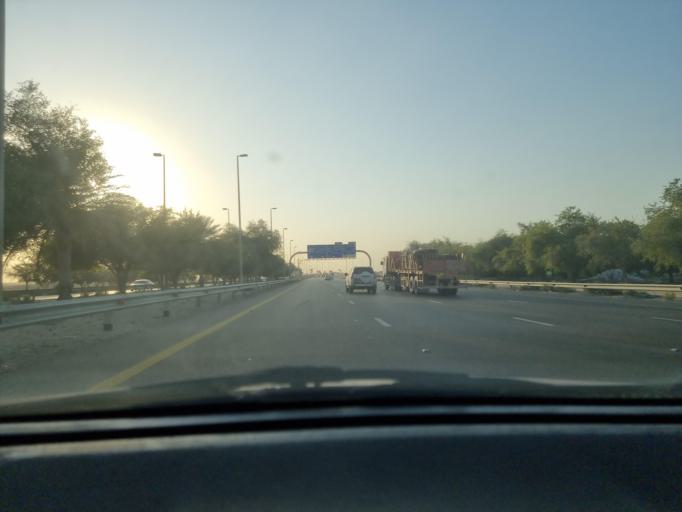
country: AE
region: Abu Dhabi
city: Abu Dhabi
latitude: 24.4108
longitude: 54.6843
